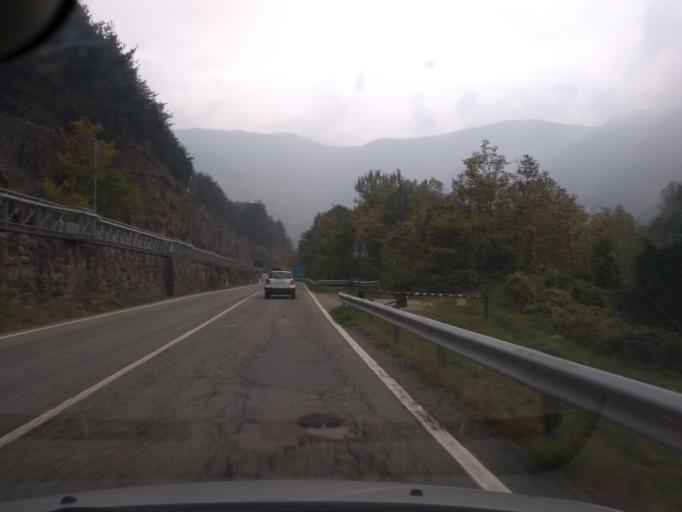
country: IT
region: Piedmont
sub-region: Provincia di Torino
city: Germagnano
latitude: 45.2634
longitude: 7.4578
